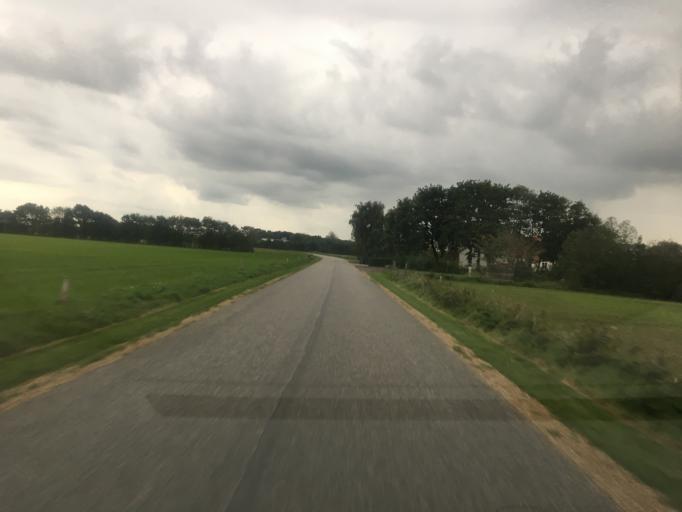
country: DK
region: South Denmark
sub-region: Tonder Kommune
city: Logumkloster
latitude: 55.0048
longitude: 9.0215
